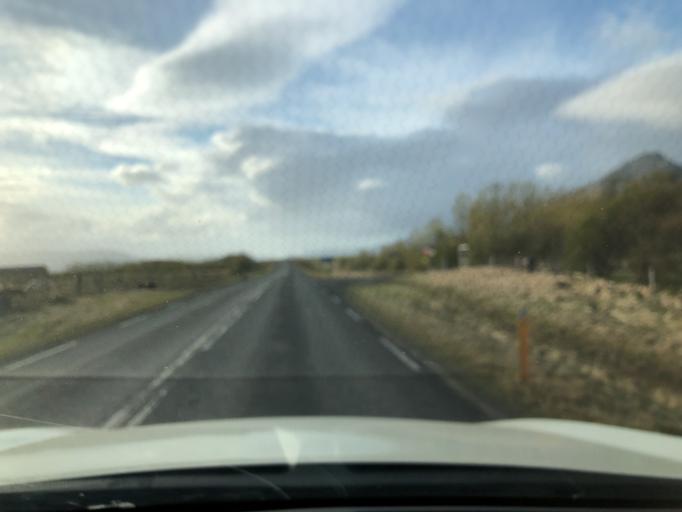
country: IS
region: East
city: Hoefn
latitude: 64.3020
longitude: -15.2039
